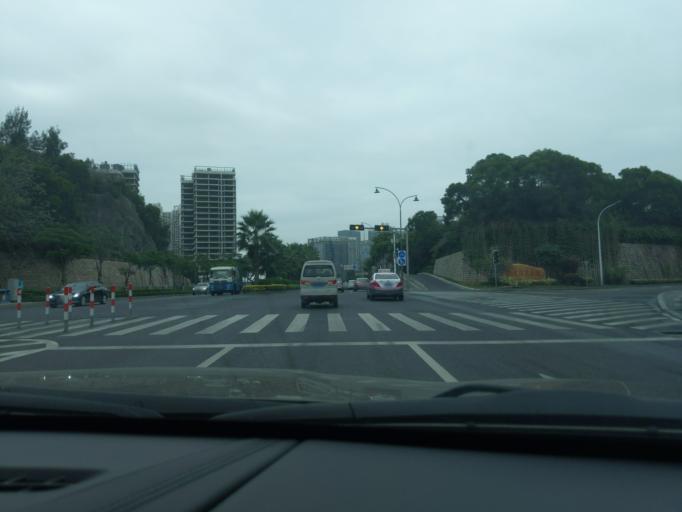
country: CN
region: Fujian
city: Liuwudian
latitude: 24.4995
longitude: 118.1713
